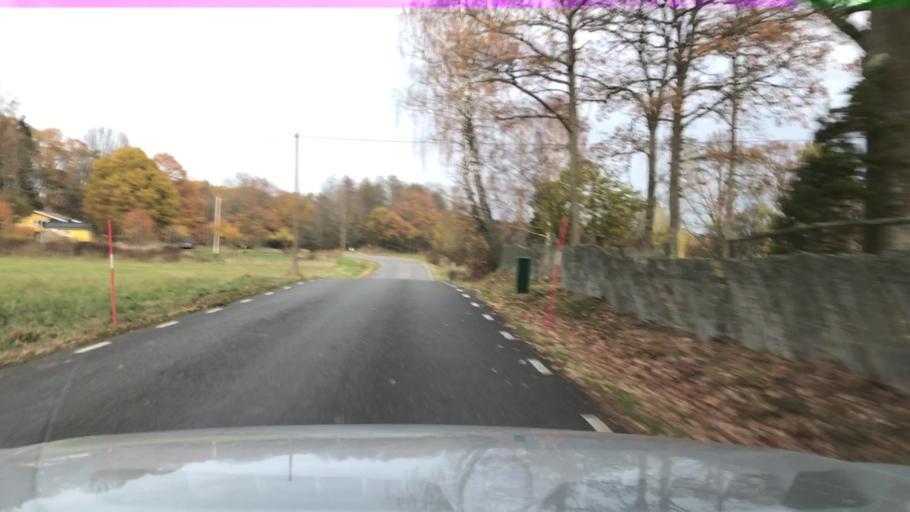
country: SE
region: OEstergoetland
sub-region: Valdemarsviks Kommun
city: Valdemarsvik
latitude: 58.2913
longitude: 16.7696
